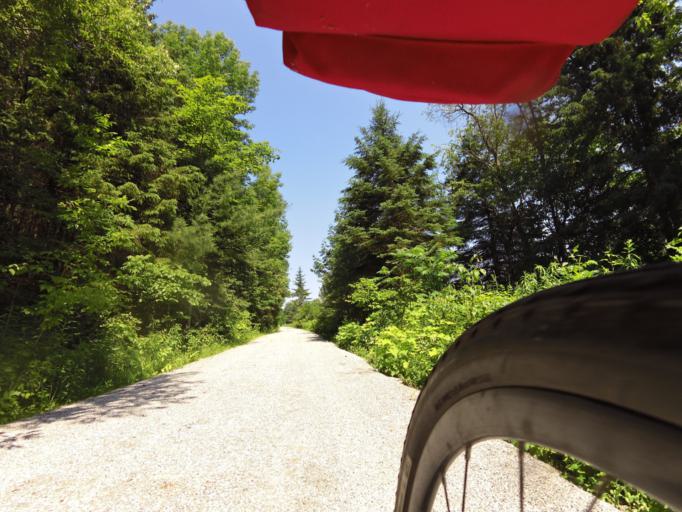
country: CA
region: Quebec
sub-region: Outaouais
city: Wakefield
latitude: 45.7857
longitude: -75.9483
